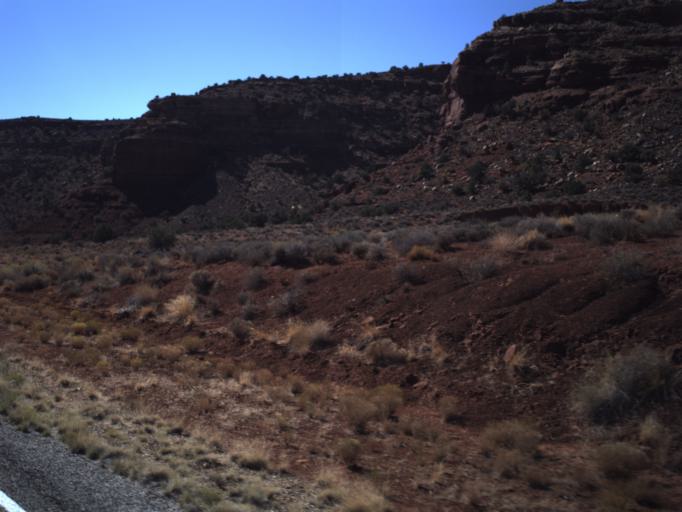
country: US
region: Utah
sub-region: San Juan County
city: Blanding
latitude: 37.7199
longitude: -110.2466
